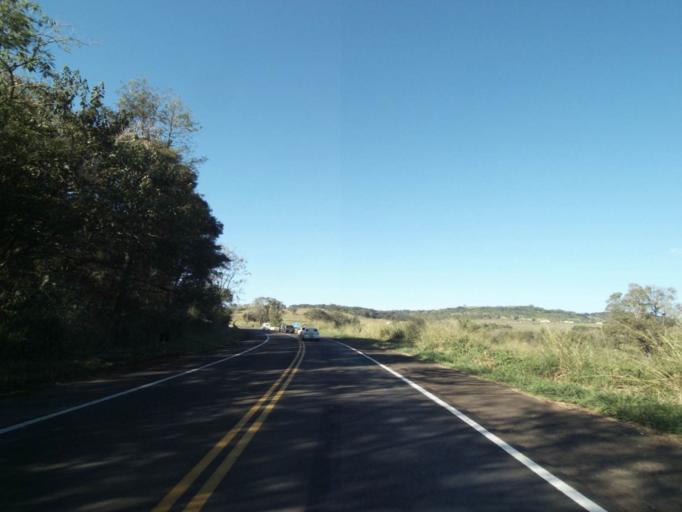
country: BR
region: Parana
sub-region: Londrina
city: Londrina
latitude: -23.6279
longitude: -51.1092
